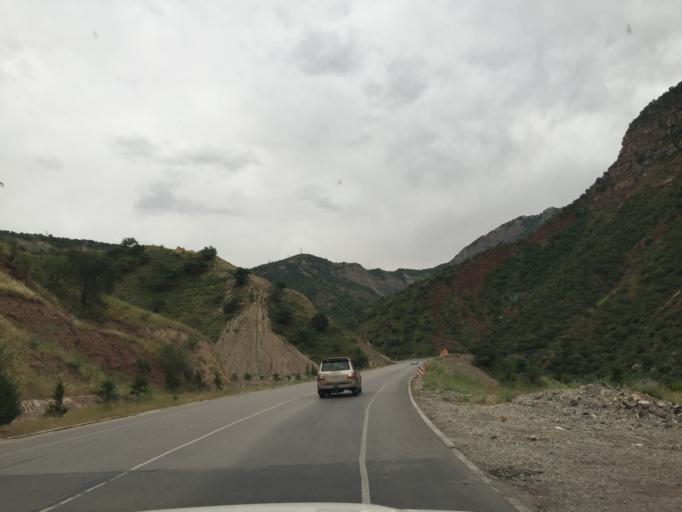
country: TJ
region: Khatlon
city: Norak
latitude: 38.3465
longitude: 69.2380
